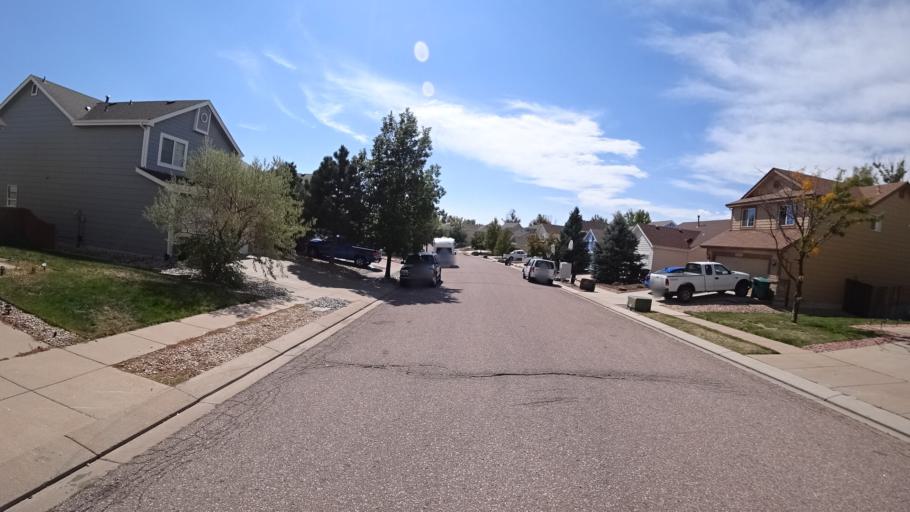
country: US
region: Colorado
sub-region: El Paso County
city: Cimarron Hills
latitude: 38.9029
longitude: -104.7120
